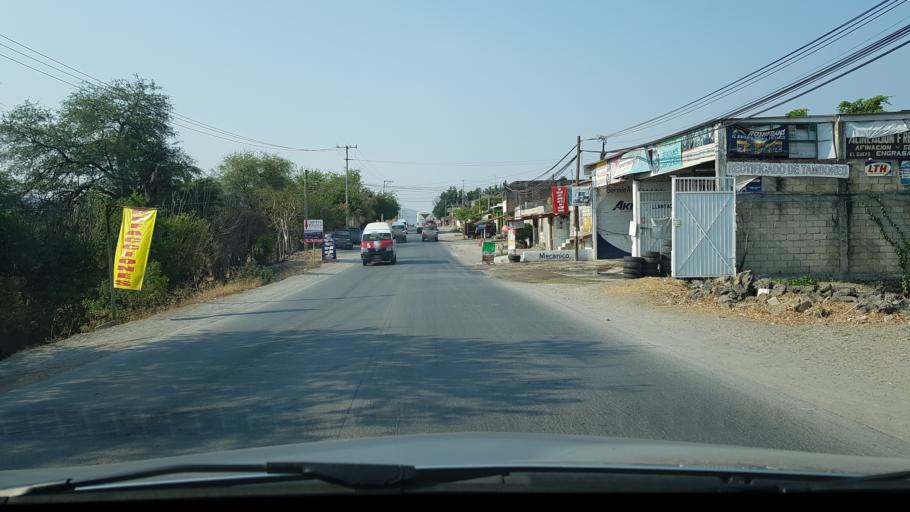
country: MX
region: Morelos
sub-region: Tlaquiltenango
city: Alfredo V. Bonfil (Chacampalco)
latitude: 18.6529
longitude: -99.1550
